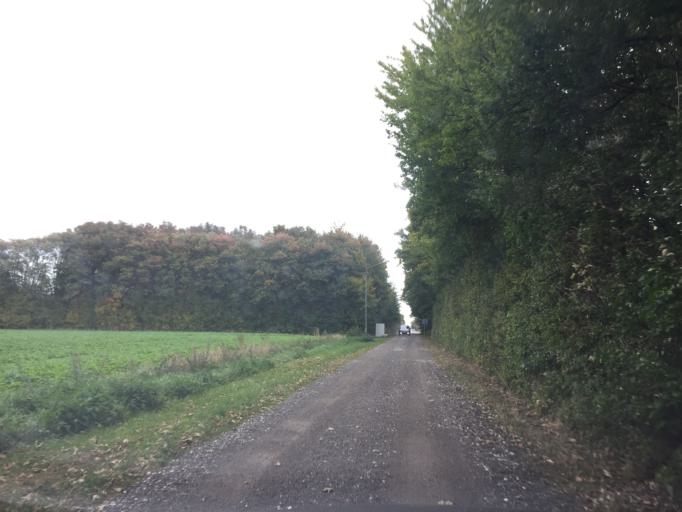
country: DK
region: Zealand
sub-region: Lolland Kommune
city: Rodbyhavn
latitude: 54.6650
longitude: 11.3493
